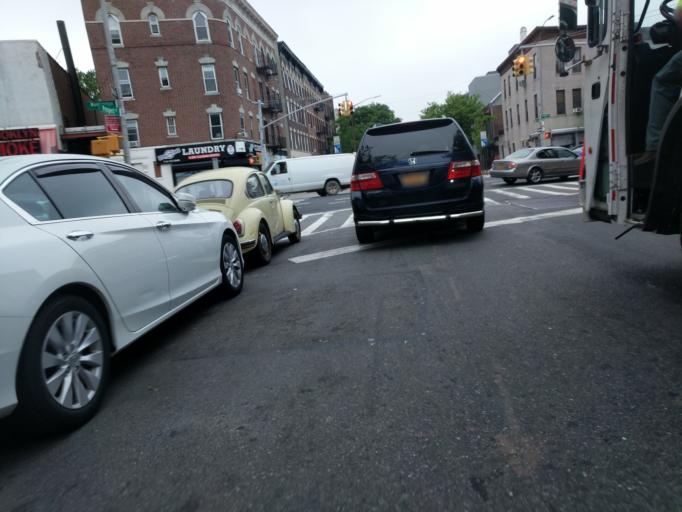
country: US
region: New York
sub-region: Kings County
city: Brooklyn
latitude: 40.6763
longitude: -73.9632
